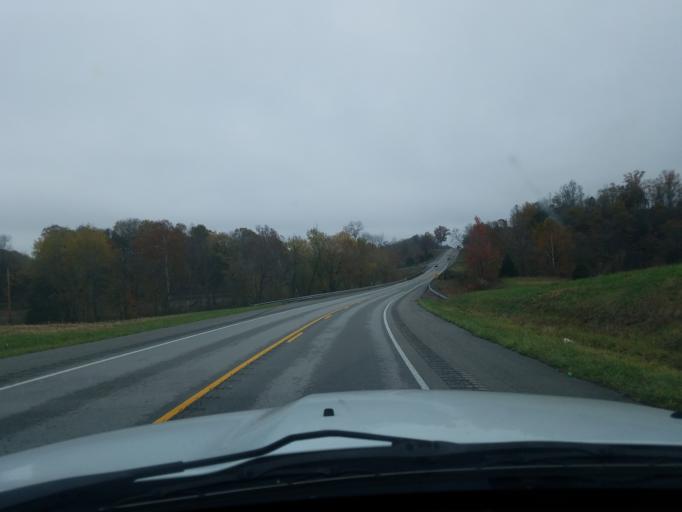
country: US
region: Kentucky
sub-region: Taylor County
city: Campbellsville
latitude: 37.3949
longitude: -85.4678
